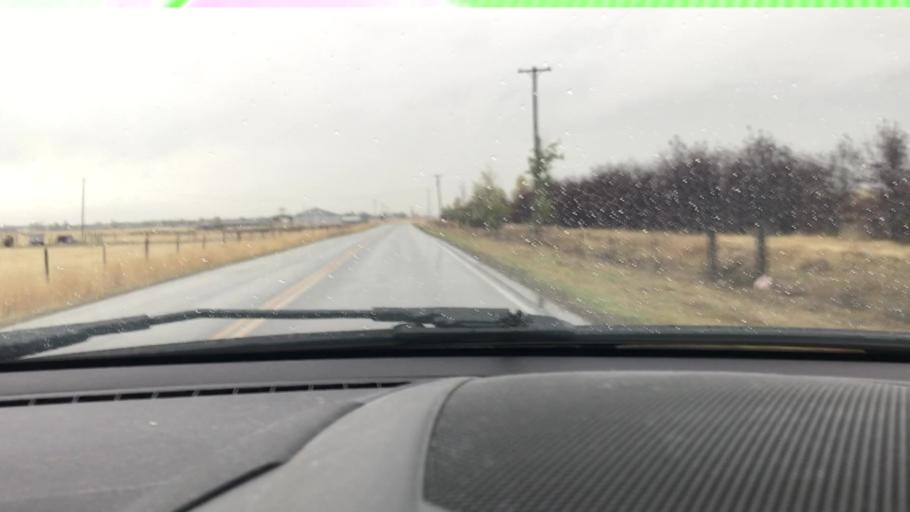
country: US
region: Montana
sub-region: Gallatin County
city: Belgrade
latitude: 45.7520
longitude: -111.1646
